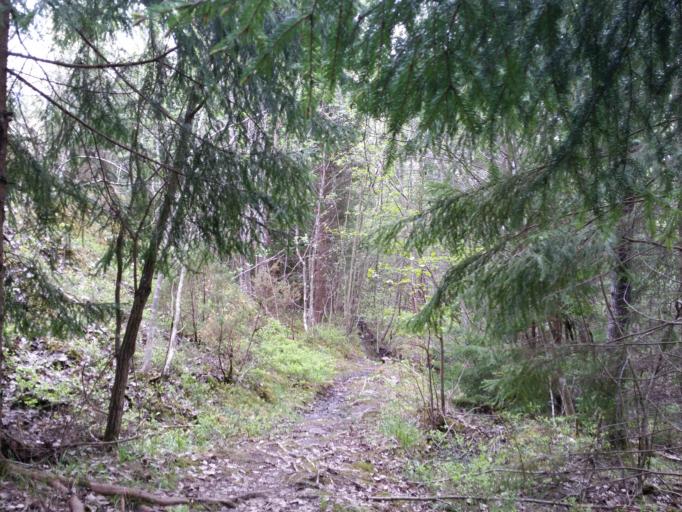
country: SE
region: Stockholm
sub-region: Sollentuna Kommun
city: Sollentuna
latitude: 59.4698
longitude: 17.9424
